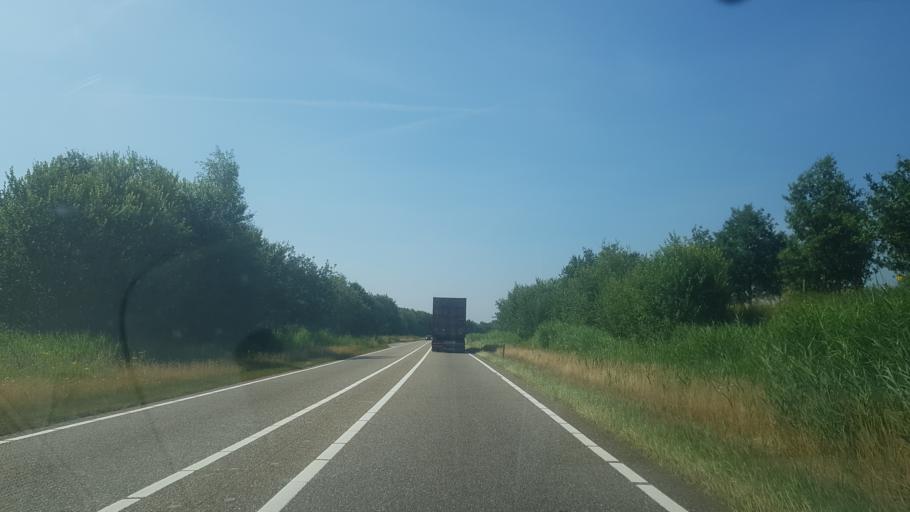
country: NL
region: North Brabant
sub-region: Gemeente Laarbeek
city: Aarle-Rixtel
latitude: 51.5144
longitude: 5.6612
